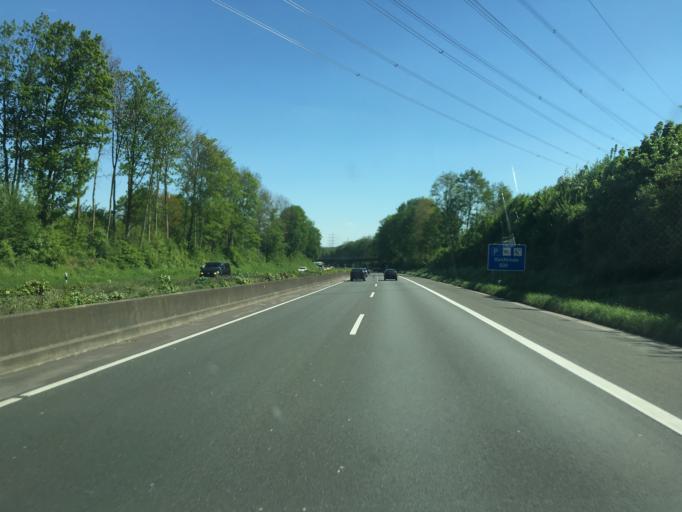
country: DE
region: North Rhine-Westphalia
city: Castrop-Rauxel
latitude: 51.5439
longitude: 7.3615
